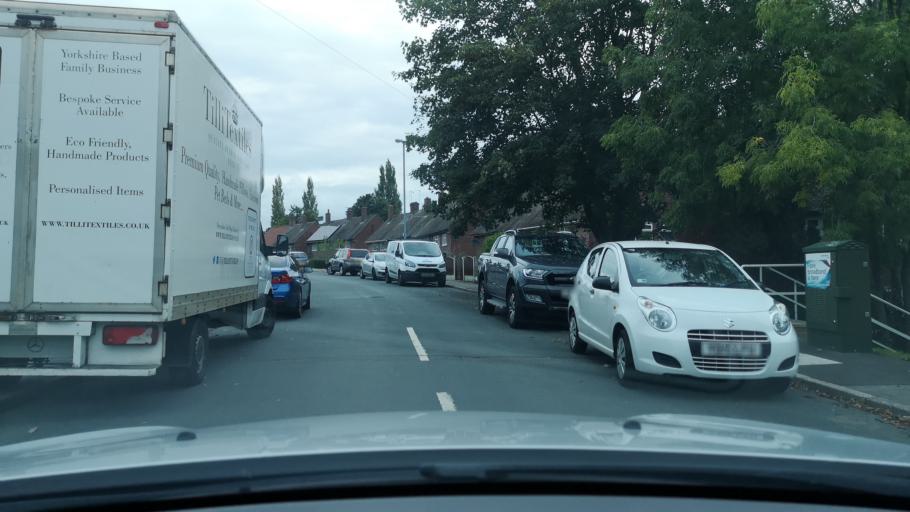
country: GB
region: England
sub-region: City and Borough of Wakefield
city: Low Ackworth
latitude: 53.6454
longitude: -1.3351
